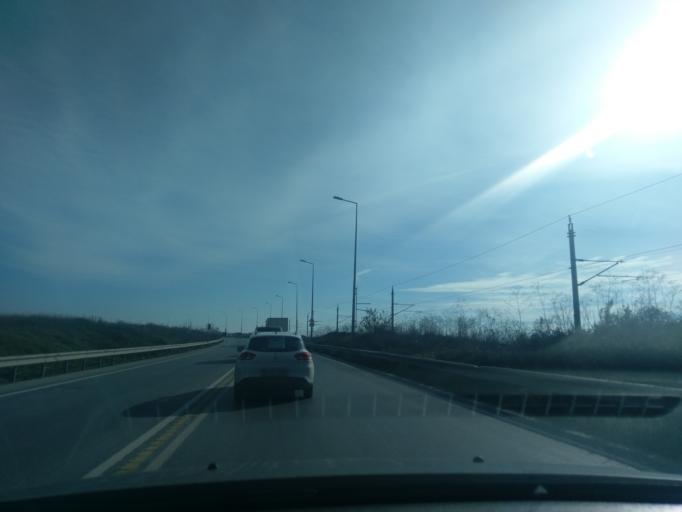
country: TR
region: Istanbul
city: Esenyurt
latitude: 41.0576
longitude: 28.7037
